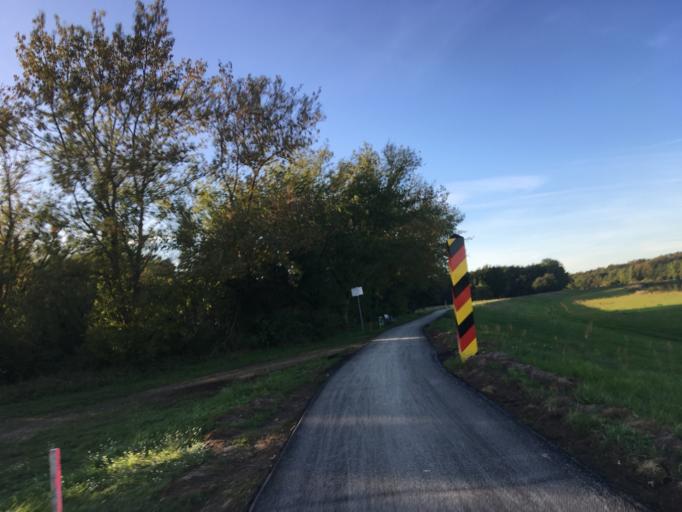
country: DE
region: Brandenburg
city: Forst
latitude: 51.7167
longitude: 14.6798
